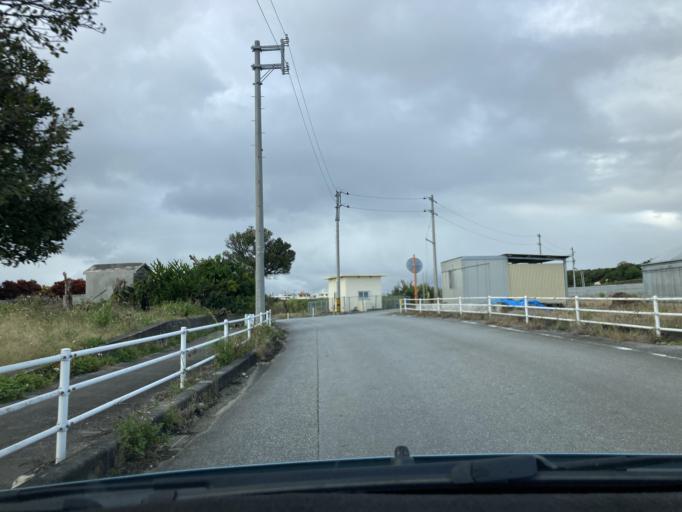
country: JP
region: Okinawa
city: Itoman
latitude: 26.1265
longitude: 127.6866
